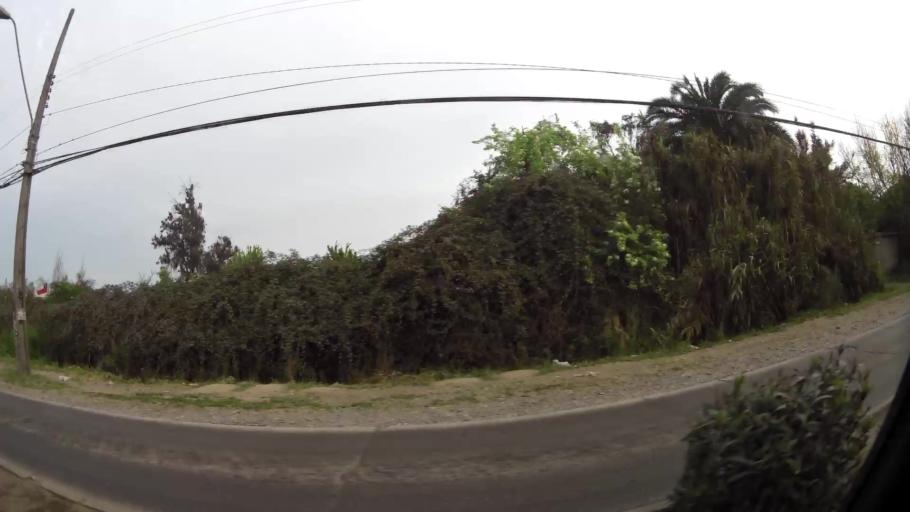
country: CL
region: Santiago Metropolitan
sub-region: Provincia de Santiago
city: Lo Prado
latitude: -33.5251
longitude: -70.7688
